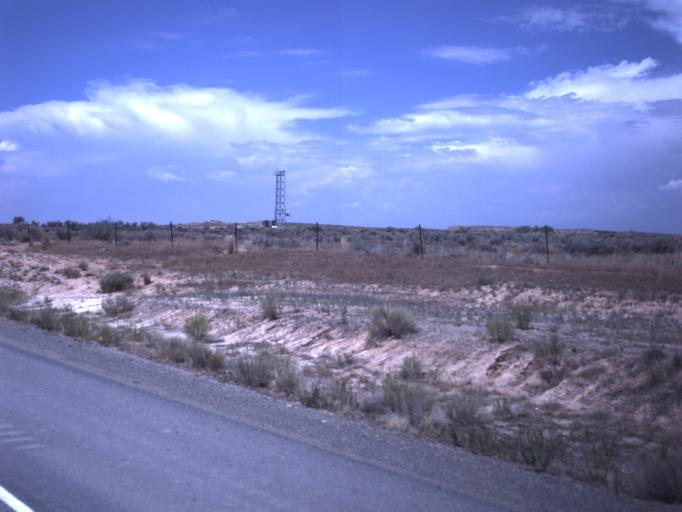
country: US
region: Utah
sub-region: Uintah County
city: Maeser
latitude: 40.3146
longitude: -109.7367
